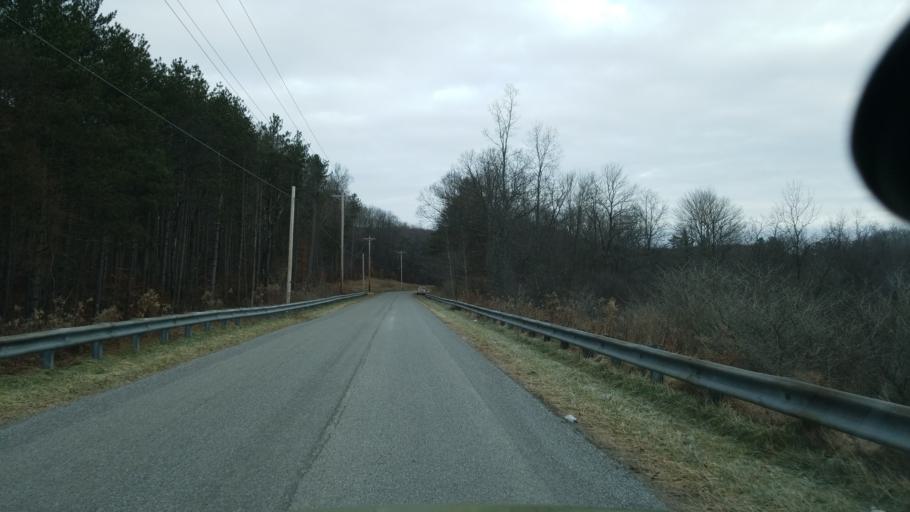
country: US
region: Pennsylvania
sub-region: Clearfield County
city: Treasure Lake
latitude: 41.1230
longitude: -78.6166
